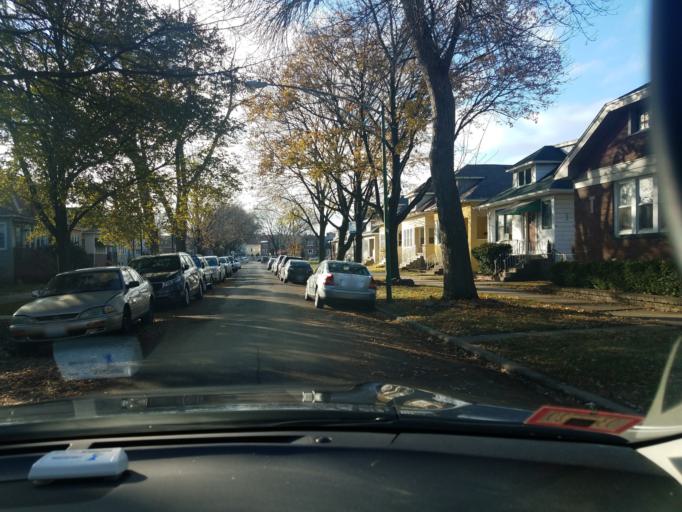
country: US
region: Illinois
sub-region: Cook County
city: Lincolnwood
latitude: 41.9650
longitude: -87.7316
